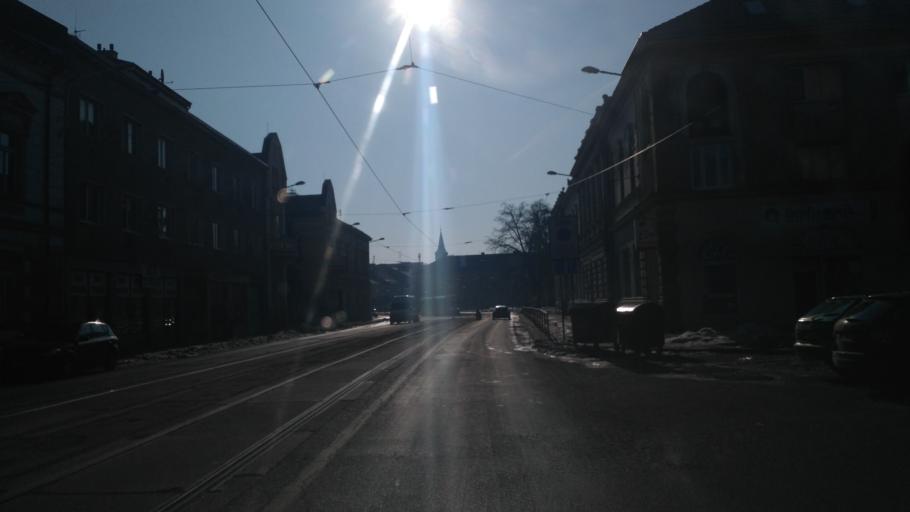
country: SK
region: Kosicky
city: Kosice
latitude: 48.7286
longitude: 21.2527
